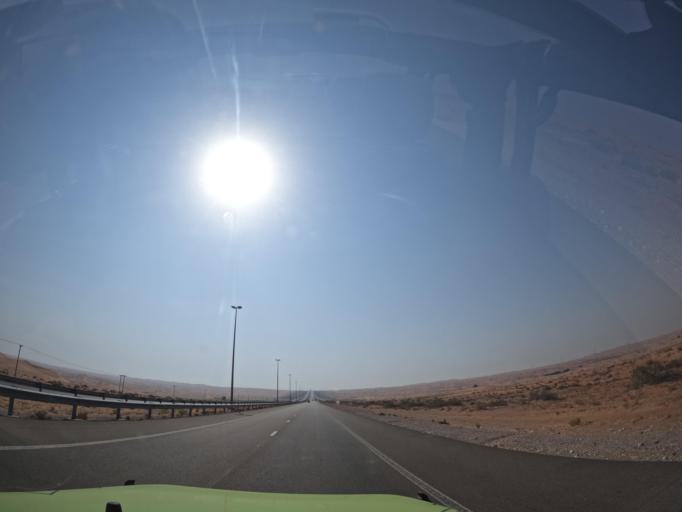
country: OM
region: Al Buraimi
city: Al Buraymi
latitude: 24.4437
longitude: 55.6611
